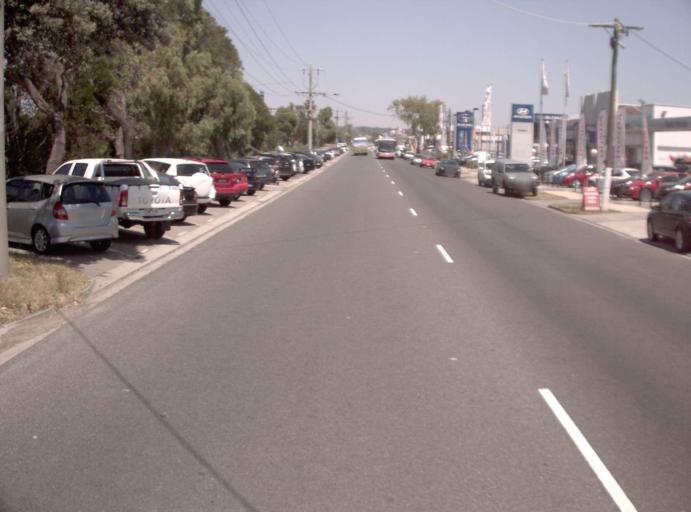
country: AU
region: Victoria
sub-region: Frankston
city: Frankston East
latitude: -38.1275
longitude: 145.1326
